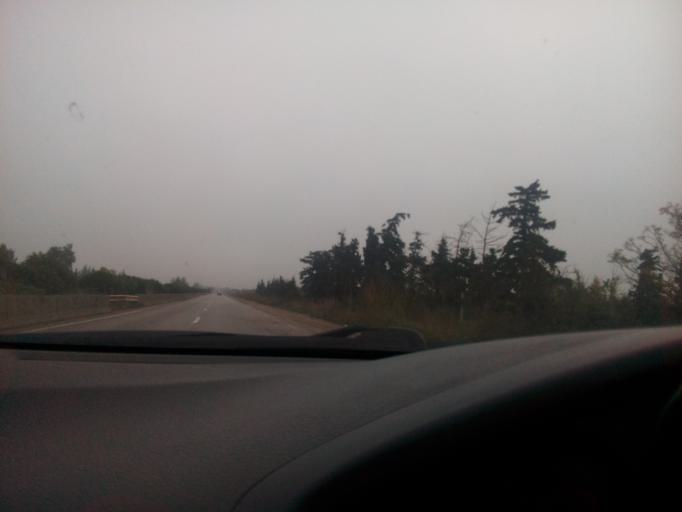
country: DZ
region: Oran
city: Bou Tlelis
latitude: 35.5665
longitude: -0.8971
